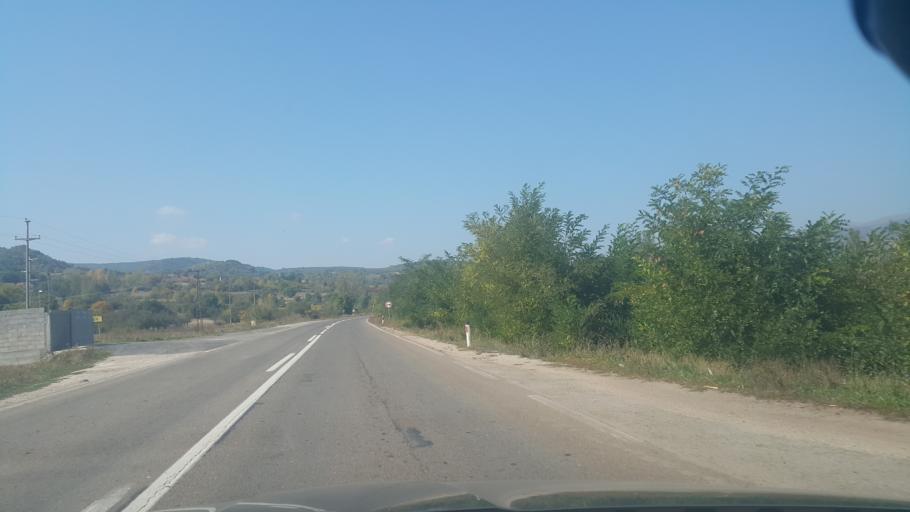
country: RS
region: Central Serbia
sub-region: Pirotski Okrug
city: Bela Palanka
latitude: 43.2339
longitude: 22.2742
